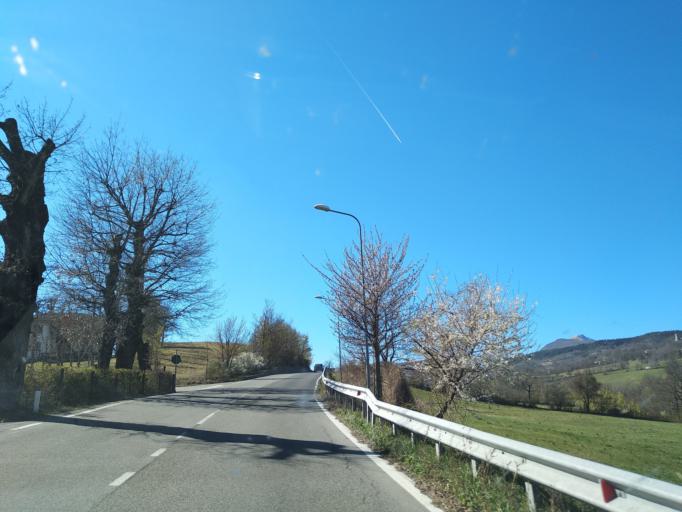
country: IT
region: Emilia-Romagna
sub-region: Provincia di Reggio Emilia
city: Castelnovo ne'Monti
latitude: 44.4243
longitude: 10.3806
